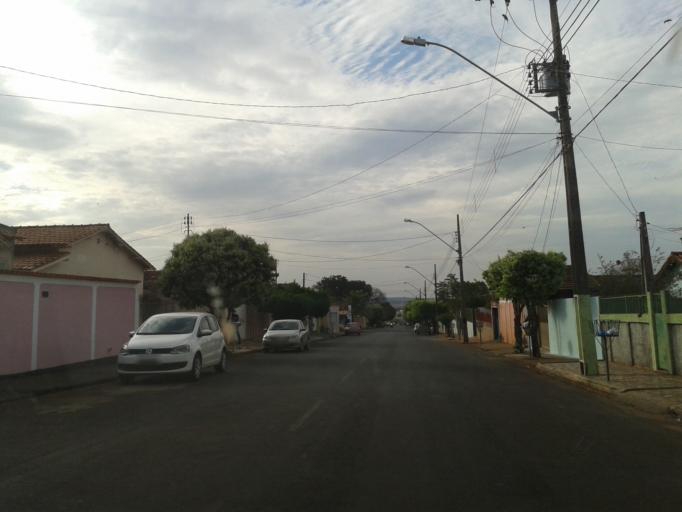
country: BR
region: Minas Gerais
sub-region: Ituiutaba
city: Ituiutaba
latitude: -18.9878
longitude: -49.4500
